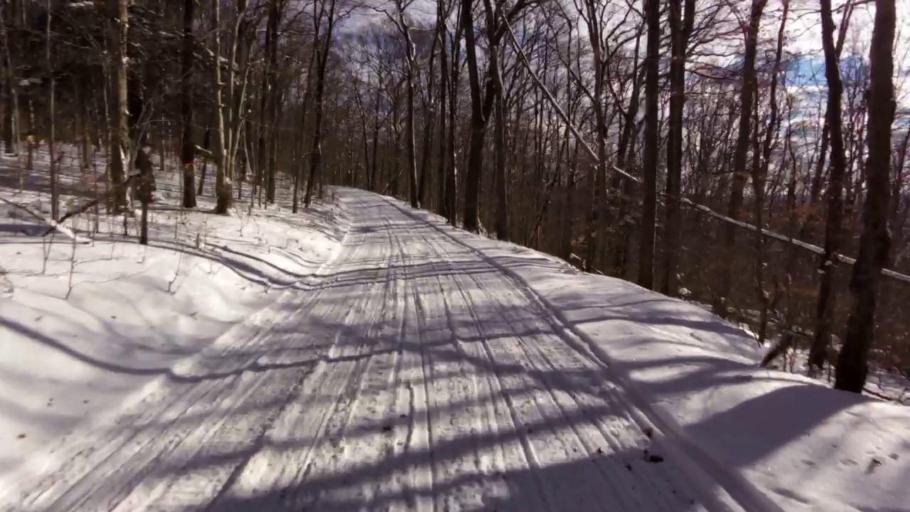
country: US
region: New York
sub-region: Cattaraugus County
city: Salamanca
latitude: 42.0710
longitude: -78.6783
